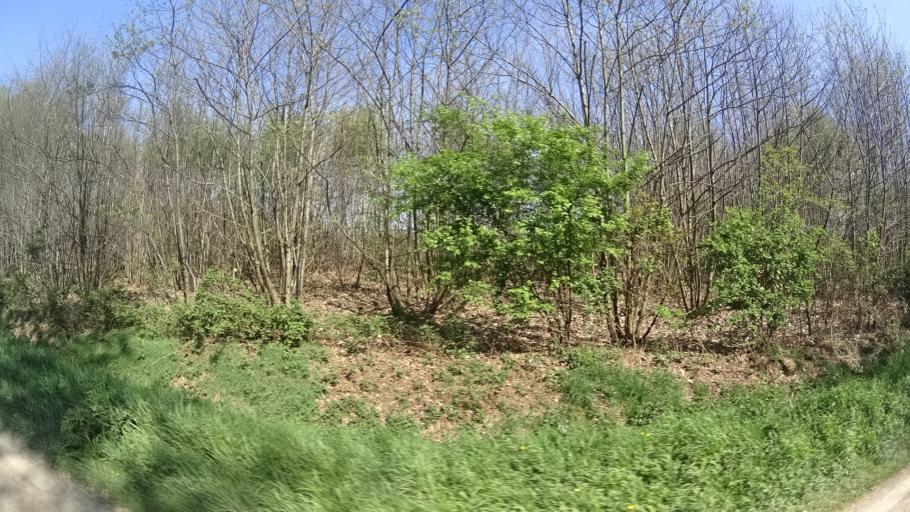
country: FR
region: Pays de la Loire
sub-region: Departement de la Loire-Atlantique
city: Saint-Nicolas-de-Redon
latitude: 47.6186
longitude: -2.0414
